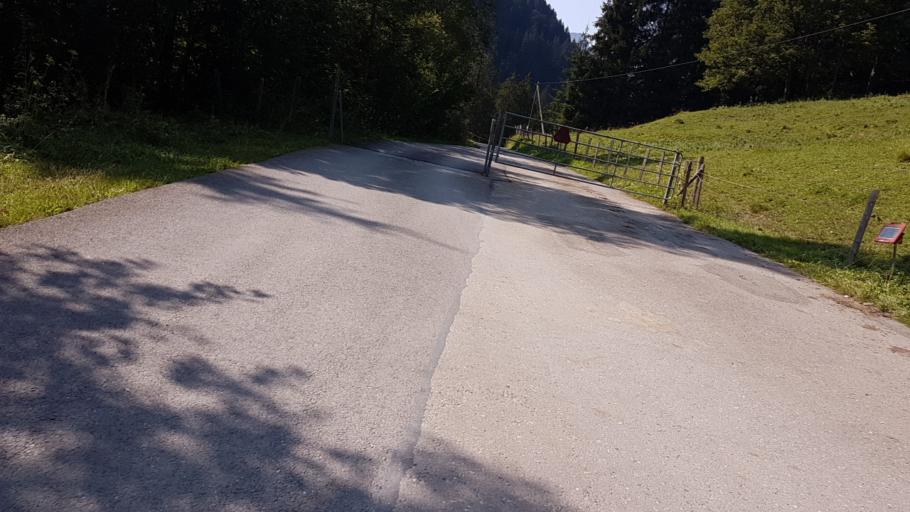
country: CH
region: Bern
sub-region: Frutigen-Niedersimmental District
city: Aeschi
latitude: 46.6274
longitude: 7.7522
